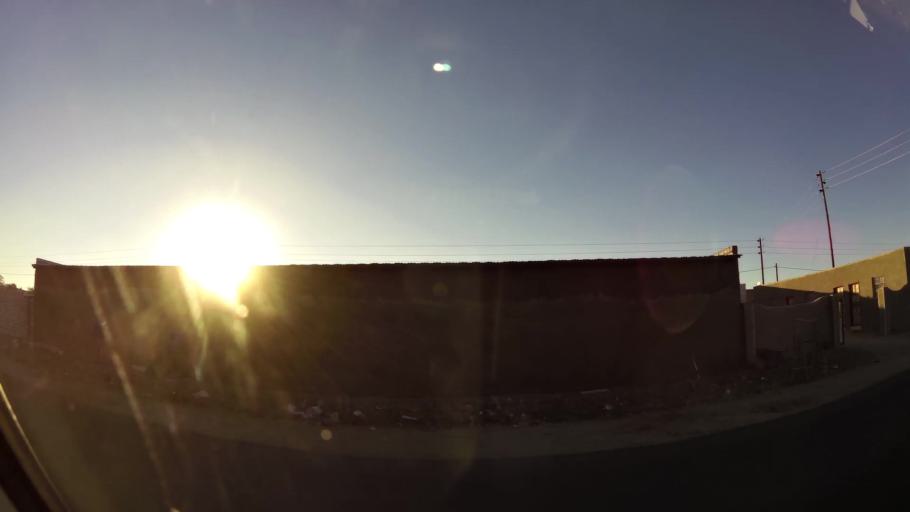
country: ZA
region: Limpopo
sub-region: Capricorn District Municipality
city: Polokwane
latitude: -23.8350
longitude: 29.3647
